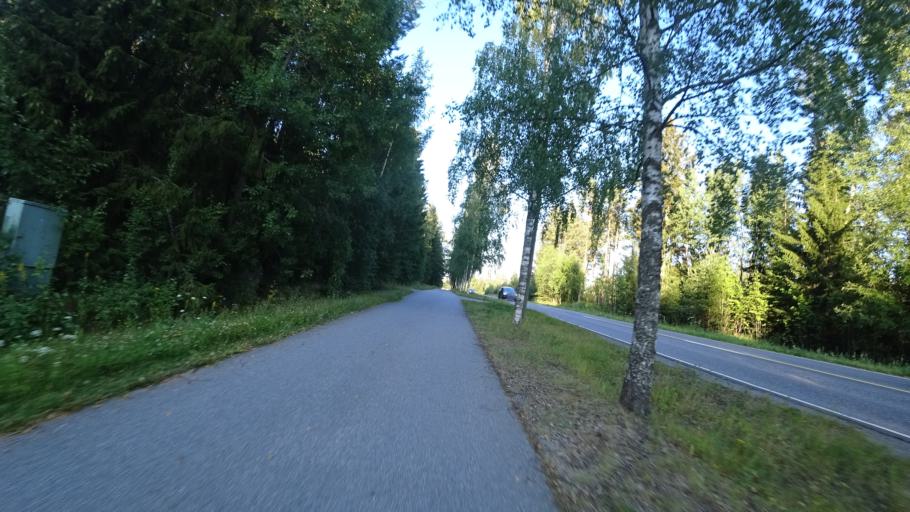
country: FI
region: Pirkanmaa
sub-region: Tampere
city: Nokia
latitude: 61.4663
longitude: 23.4286
